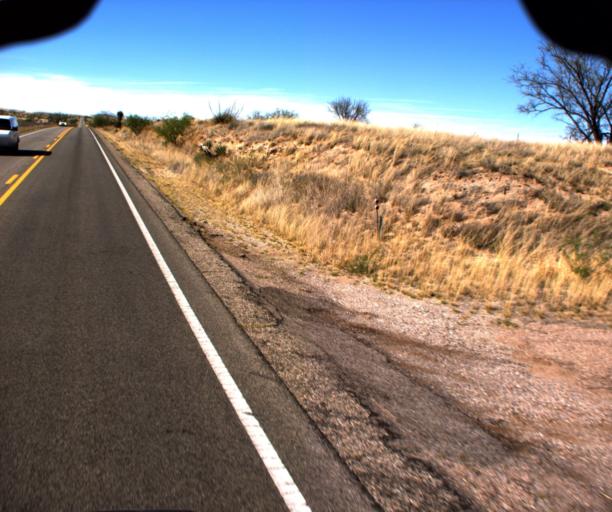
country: US
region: Arizona
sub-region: Pima County
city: Corona de Tucson
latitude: 31.7474
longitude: -110.6694
